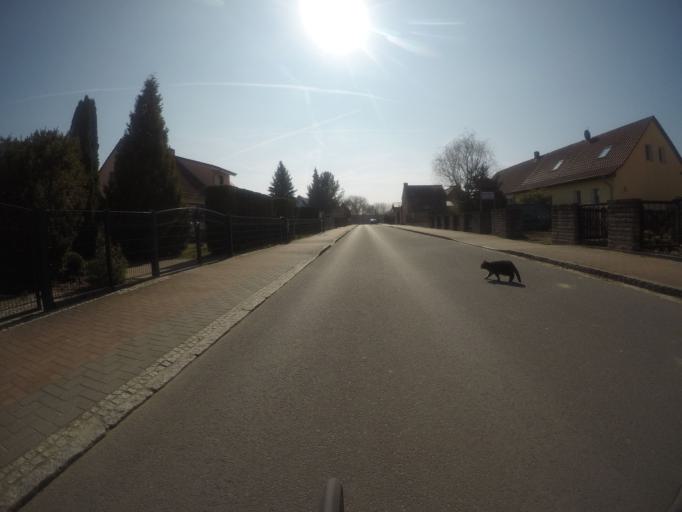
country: DE
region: Brandenburg
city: Erkner
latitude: 52.3908
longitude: 13.7127
